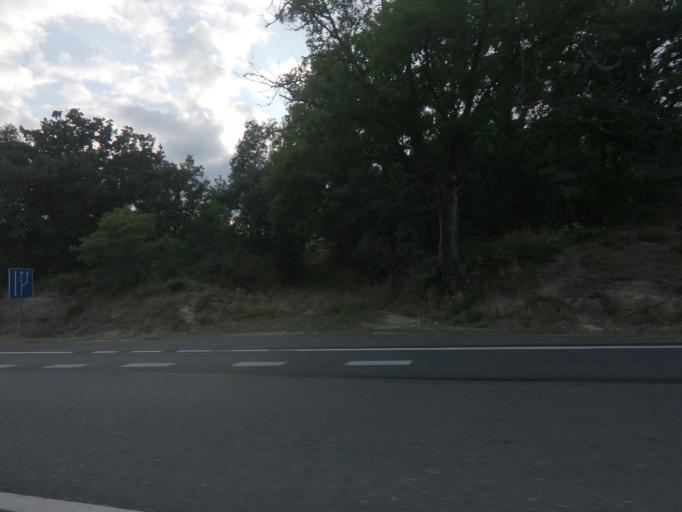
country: ES
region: Galicia
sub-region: Provincia de Ourense
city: Taboadela
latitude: 42.2504
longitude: -7.8374
